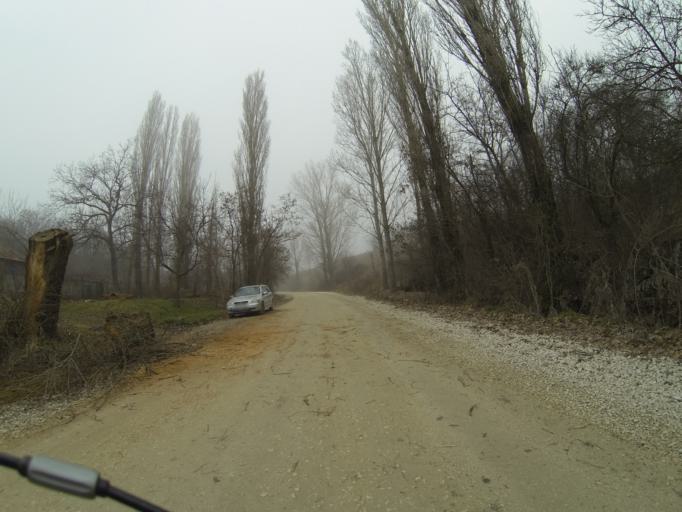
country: RO
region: Mehedinti
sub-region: Comuna Balacita
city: Gvardinita
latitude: 44.4097
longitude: 23.1434
